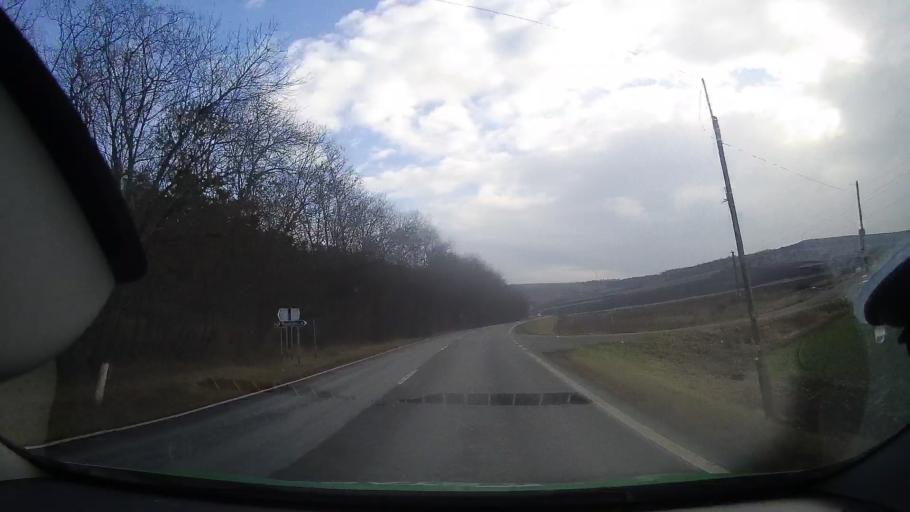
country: RO
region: Mures
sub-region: Comuna Cucerdea
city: Cucerdea
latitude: 46.3674
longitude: 24.2647
